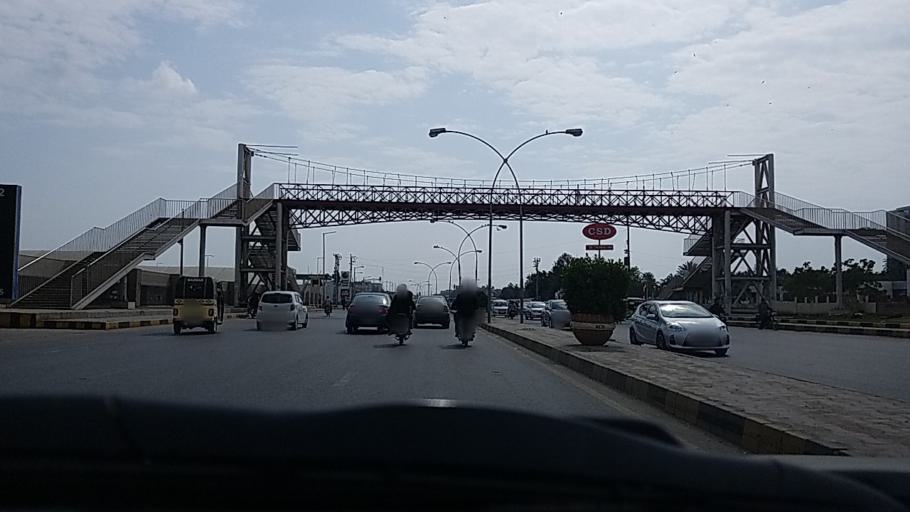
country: PK
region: Sindh
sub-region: Karachi District
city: Karachi
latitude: 24.8543
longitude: 67.0519
